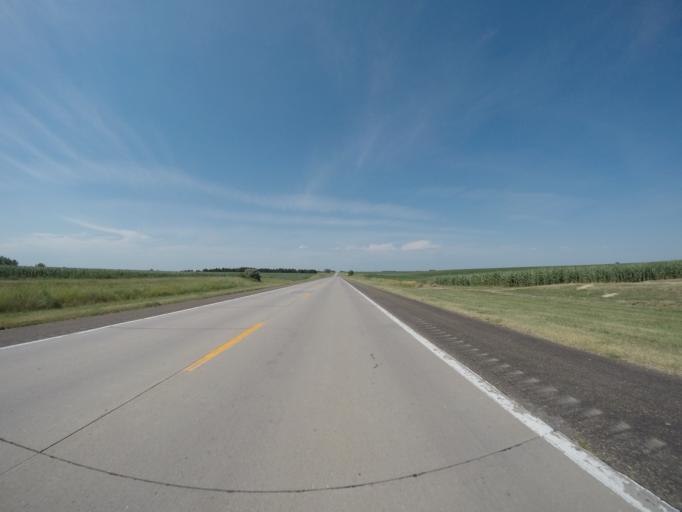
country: US
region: Nebraska
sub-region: Adams County
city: Hastings
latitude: 40.3812
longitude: -98.4397
